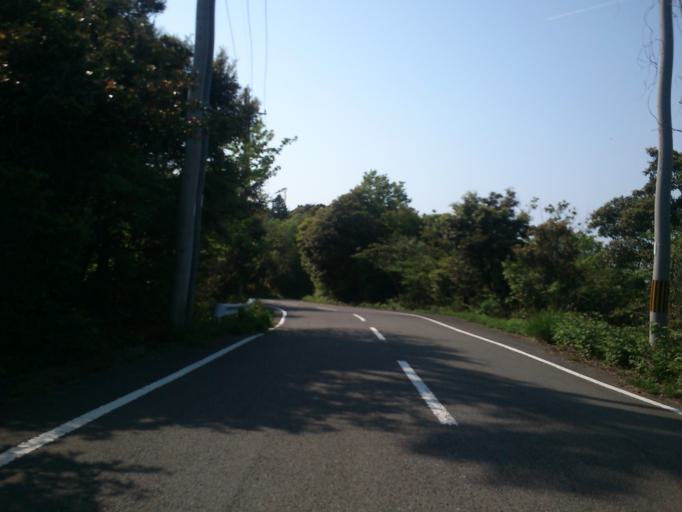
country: JP
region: Kyoto
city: Miyazu
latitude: 35.7465
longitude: 135.1716
